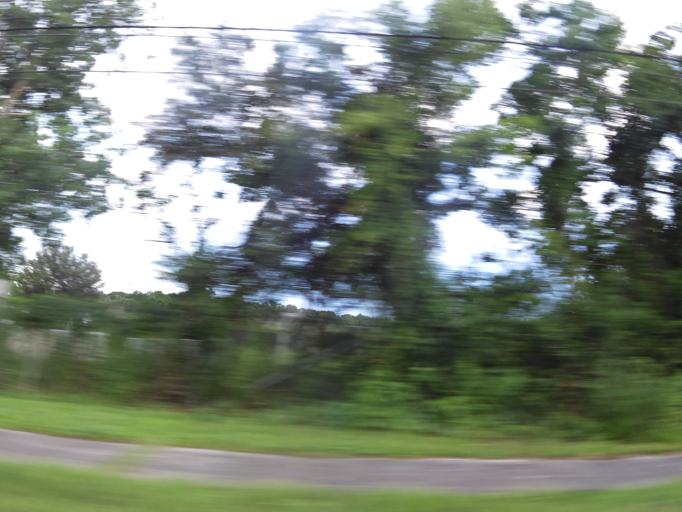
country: US
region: Florida
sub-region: Duval County
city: Jacksonville
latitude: 30.3714
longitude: -81.7879
